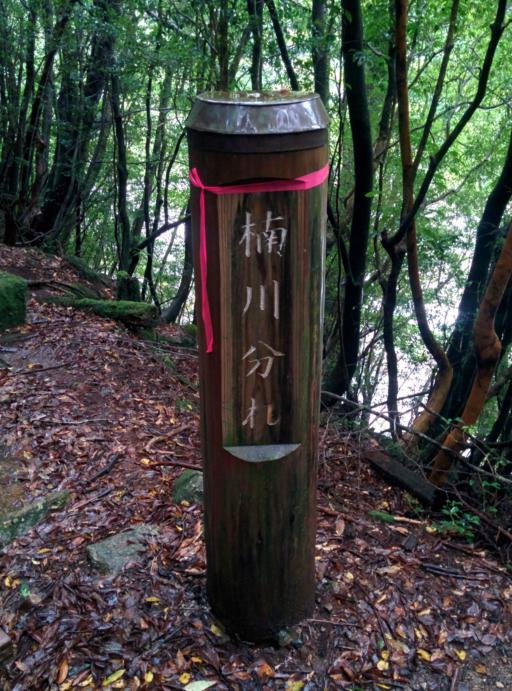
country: JP
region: Kagoshima
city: Nishinoomote
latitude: 30.3542
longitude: 130.5628
